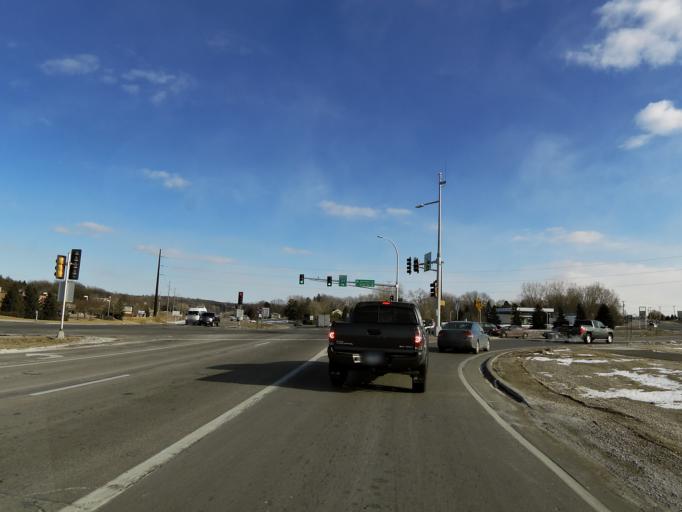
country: US
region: Minnesota
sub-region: Dakota County
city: Mendota Heights
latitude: 44.8461
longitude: -93.1243
